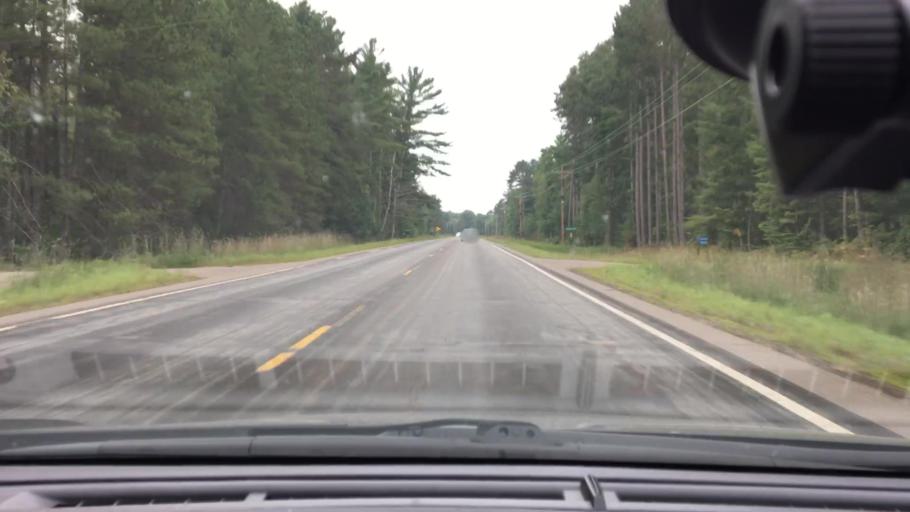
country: US
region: Minnesota
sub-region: Crow Wing County
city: Cross Lake
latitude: 46.7964
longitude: -93.9628
